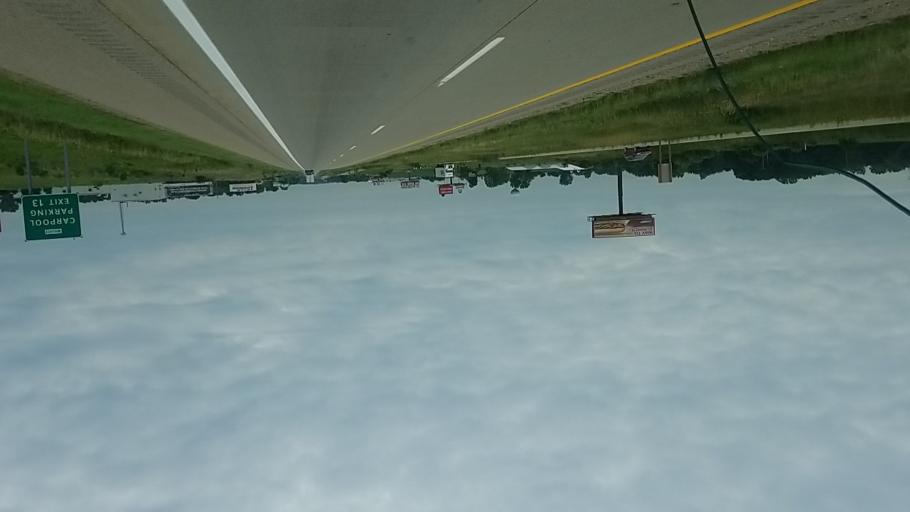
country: US
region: Michigan
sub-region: Branch County
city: Coldwater
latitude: 41.9542
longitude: -84.9737
